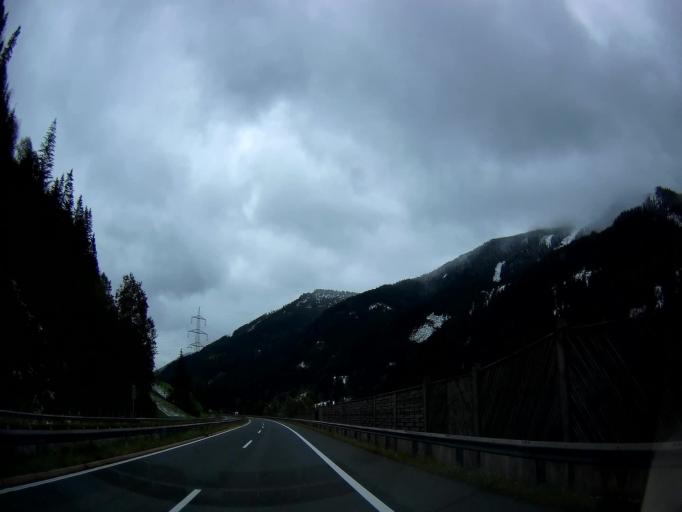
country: AT
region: Styria
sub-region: Politischer Bezirk Leoben
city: Wald am Schoberpass
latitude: 47.4598
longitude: 14.6553
